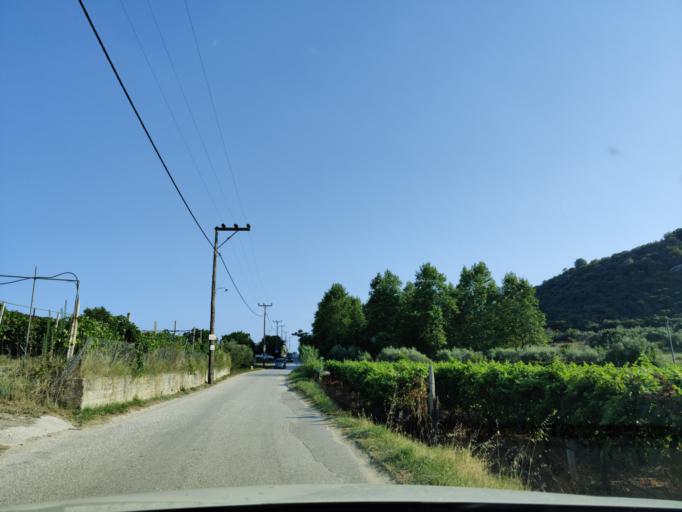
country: GR
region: East Macedonia and Thrace
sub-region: Nomos Kavalas
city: Nea Peramos
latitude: 40.8232
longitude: 24.3078
